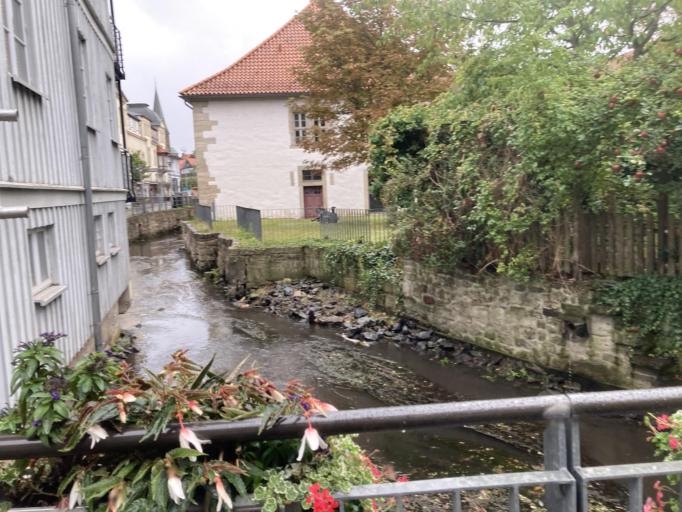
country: DE
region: Lower Saxony
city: Wolfenbuettel
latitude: 52.1623
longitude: 10.5345
